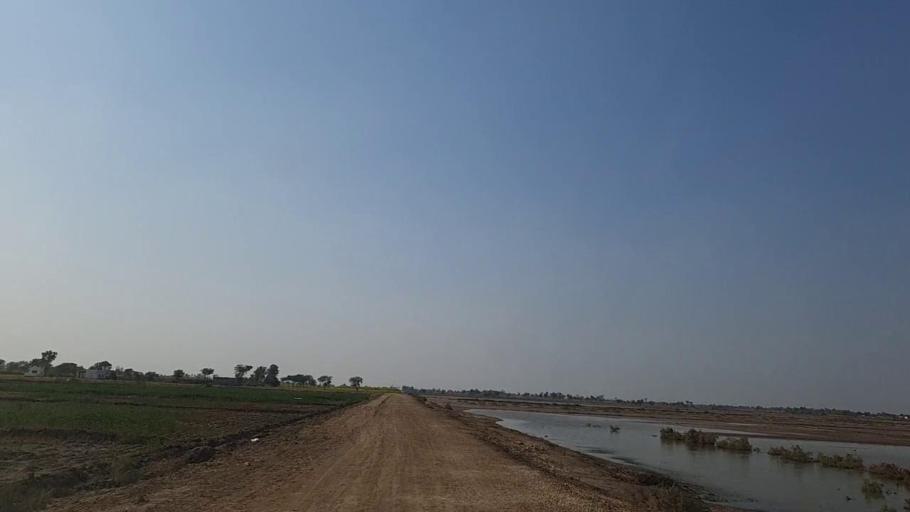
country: PK
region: Sindh
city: Daur
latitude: 26.4533
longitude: 68.2450
